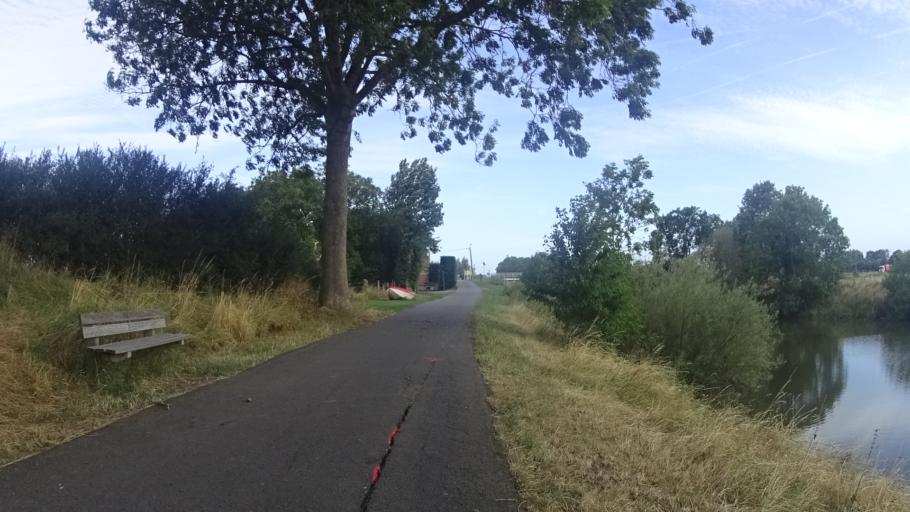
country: BE
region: Flanders
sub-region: Provincie West-Vlaanderen
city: Ieper
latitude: 50.9190
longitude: 2.8450
